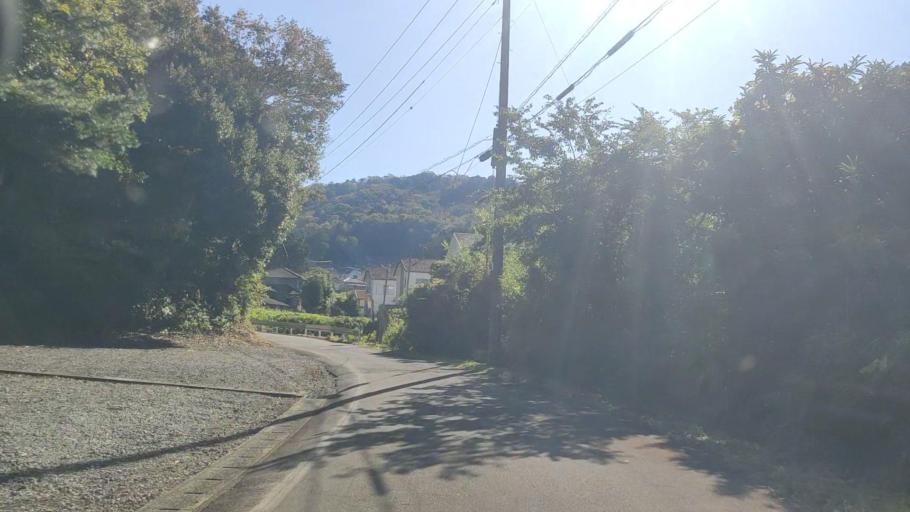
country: JP
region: Shizuoka
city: Mishima
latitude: 35.0153
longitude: 138.9564
